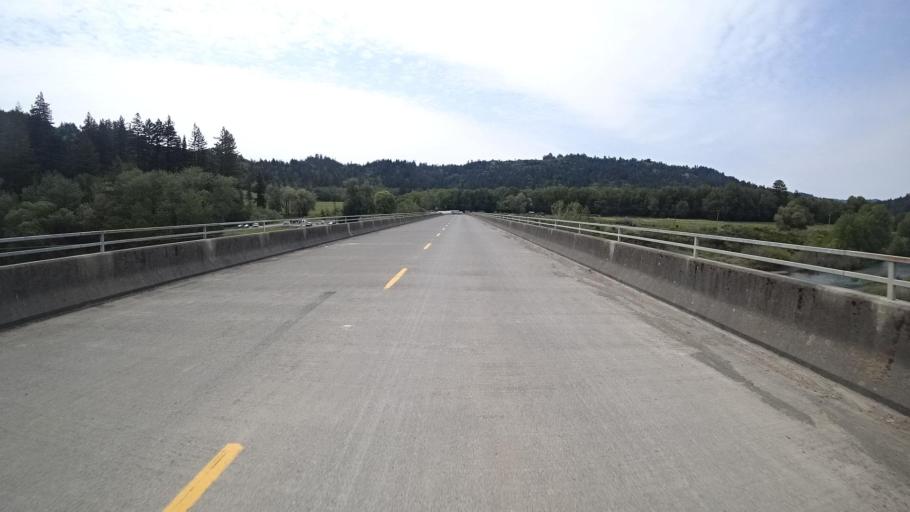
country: US
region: California
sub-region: Humboldt County
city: Redway
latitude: 40.0908
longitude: -123.7990
